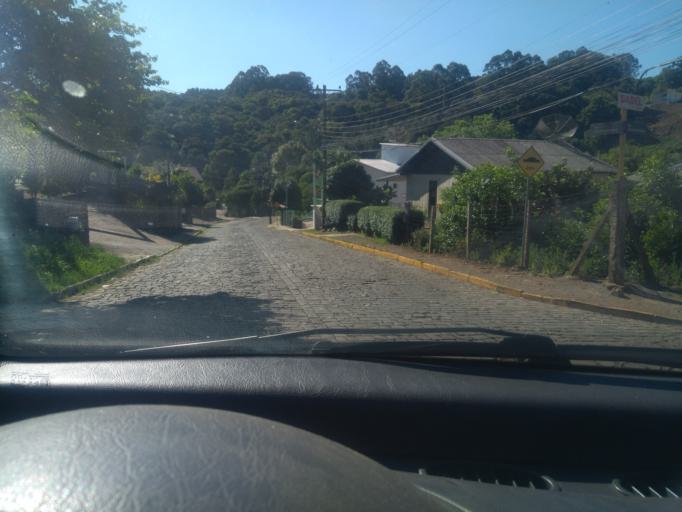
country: BR
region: Rio Grande do Sul
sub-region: Veranopolis
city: Veranopolis
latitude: -28.9369
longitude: -51.5559
